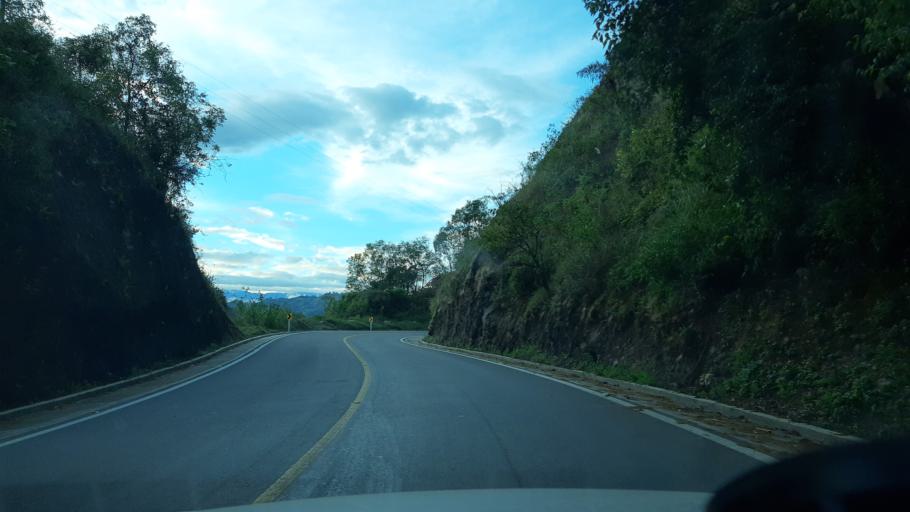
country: CO
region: Boyaca
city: Somondoco
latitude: 4.9908
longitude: -73.3503
